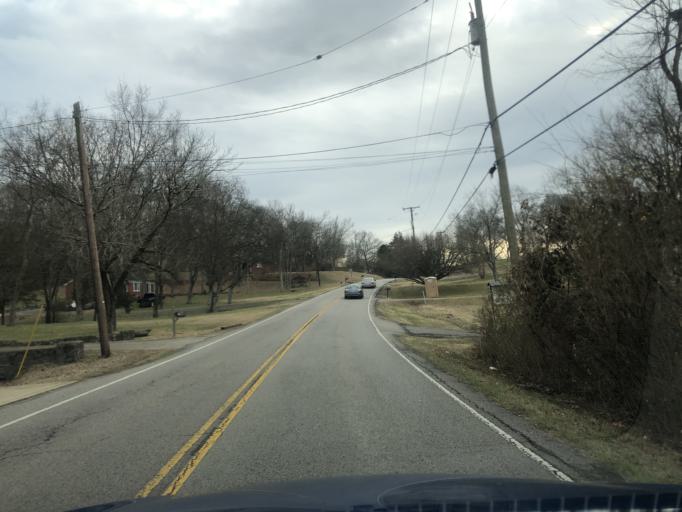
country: US
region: Tennessee
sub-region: Davidson County
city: Belle Meade
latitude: 36.1109
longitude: -86.9292
